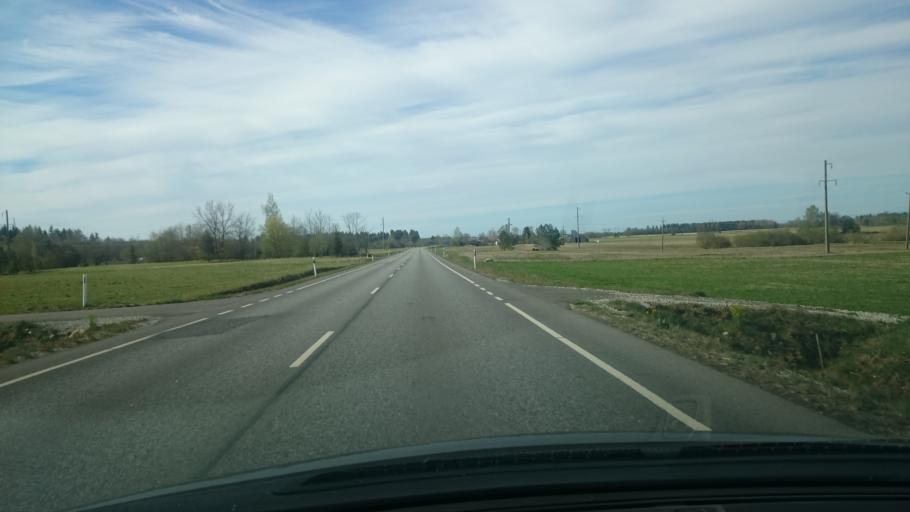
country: EE
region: Ida-Virumaa
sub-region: Johvi vald
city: Johvi
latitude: 59.2863
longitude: 27.4982
